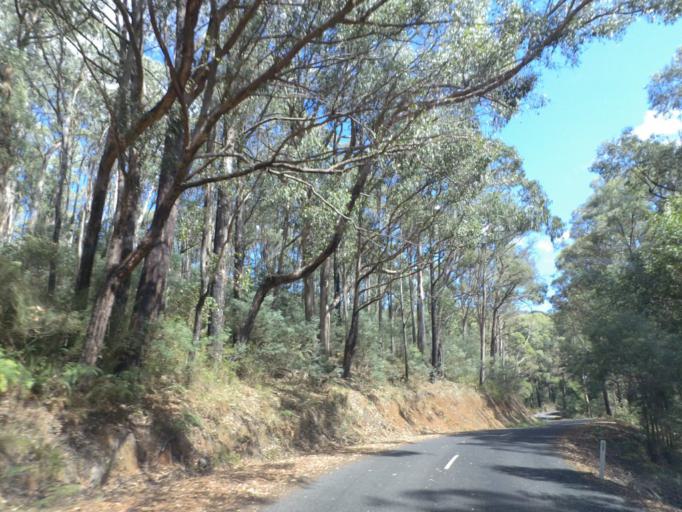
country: AU
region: Victoria
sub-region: Murrindindi
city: Alexandra
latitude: -37.3357
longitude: 145.9528
